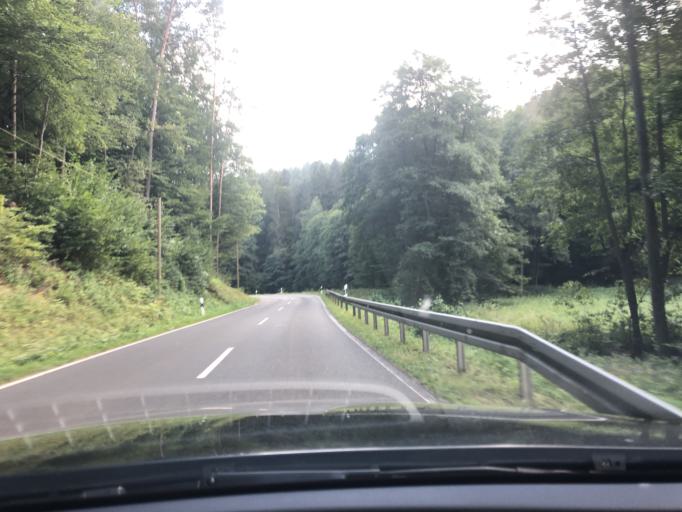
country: DE
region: Bavaria
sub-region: Regierungsbezirk Unterfranken
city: Breitbrunn
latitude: 50.0264
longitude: 10.6786
